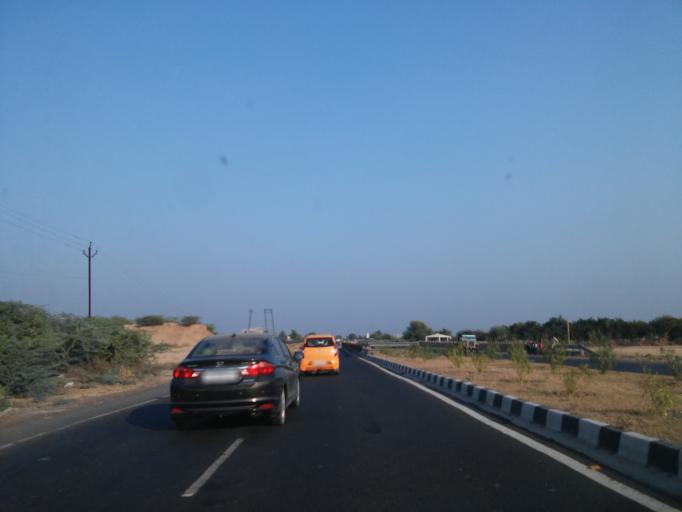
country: IN
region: Gujarat
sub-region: Ahmadabad
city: Mandal
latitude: 23.0979
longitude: 72.0918
